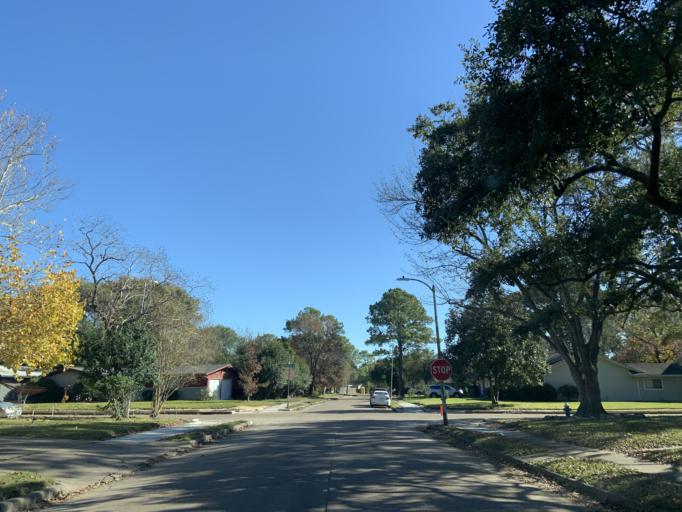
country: US
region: Texas
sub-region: Harris County
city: Bellaire
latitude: 29.6961
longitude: -95.5114
